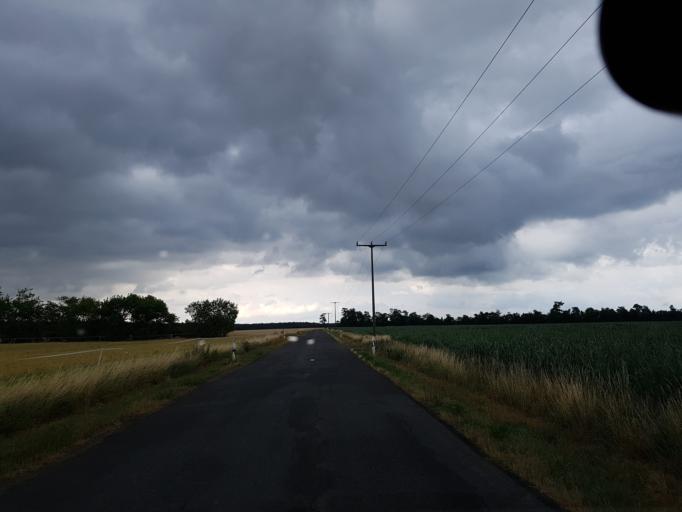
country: DE
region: Saxony-Anhalt
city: Seyda
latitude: 51.9237
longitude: 12.9253
